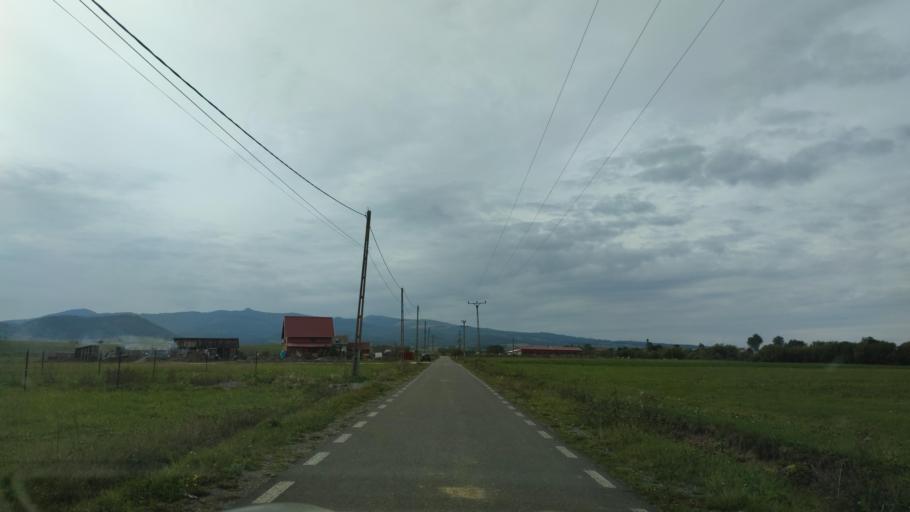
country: RO
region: Harghita
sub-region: Comuna Remetea
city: Remetea
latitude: 46.8096
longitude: 25.4260
